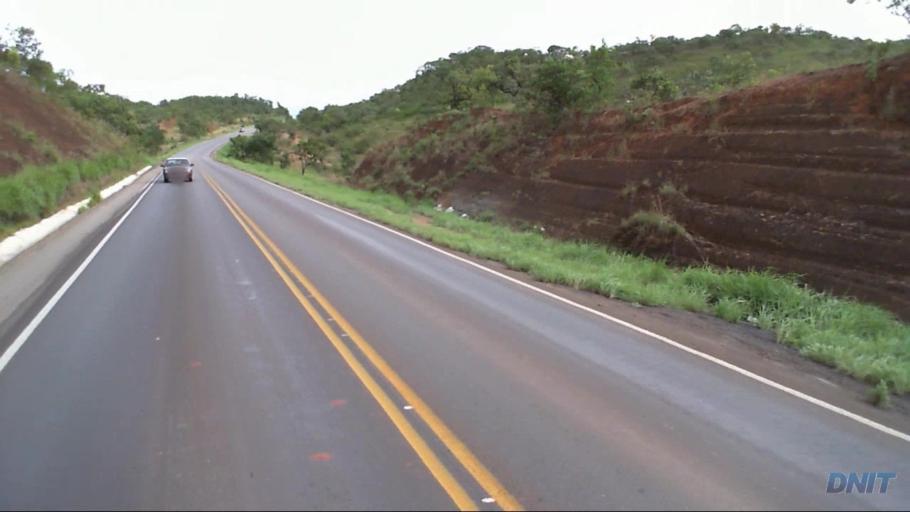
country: BR
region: Goias
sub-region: Padre Bernardo
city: Padre Bernardo
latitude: -15.2236
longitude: -48.2792
